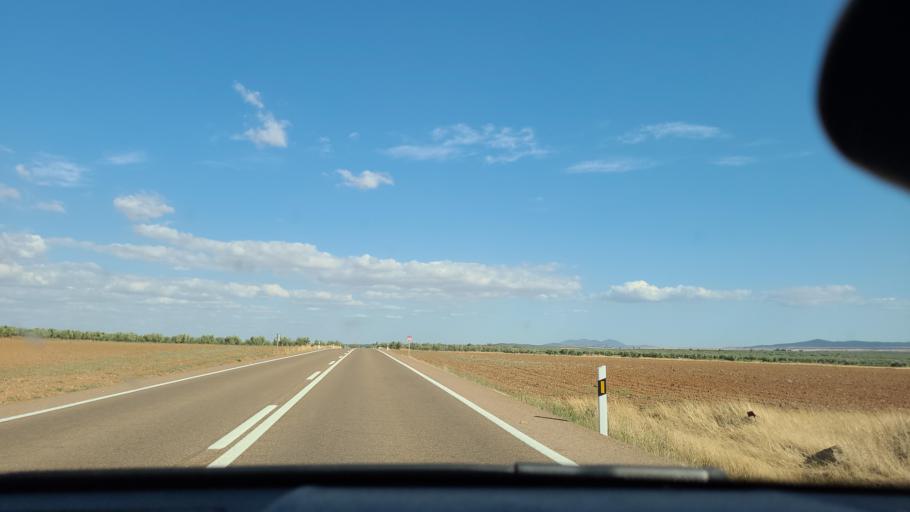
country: ES
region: Extremadura
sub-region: Provincia de Badajoz
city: Usagre
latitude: 38.3549
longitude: -6.2035
